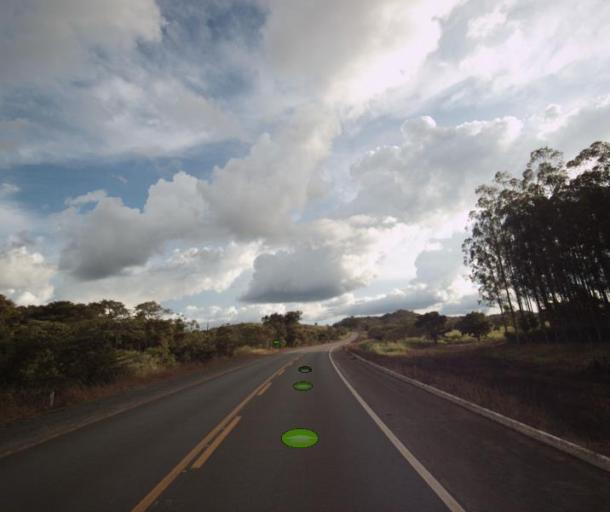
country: BR
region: Goias
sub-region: Niquelandia
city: Niquelandia
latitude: -14.5754
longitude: -48.5666
